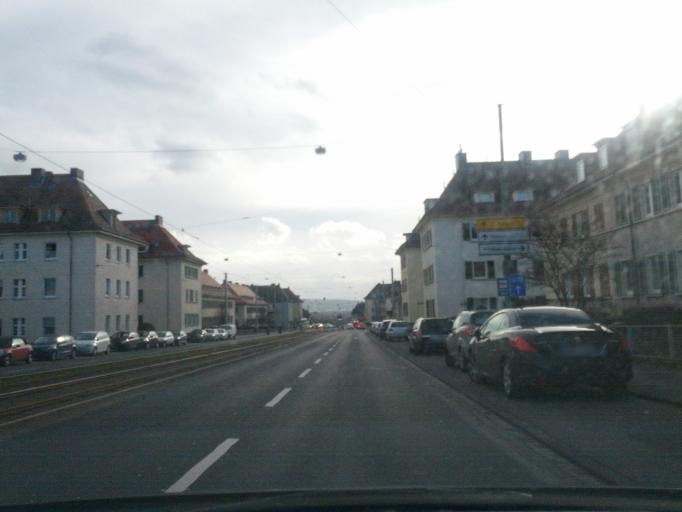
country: DE
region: Hesse
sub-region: Regierungsbezirk Kassel
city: Kassel
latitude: 51.3327
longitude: 9.5133
